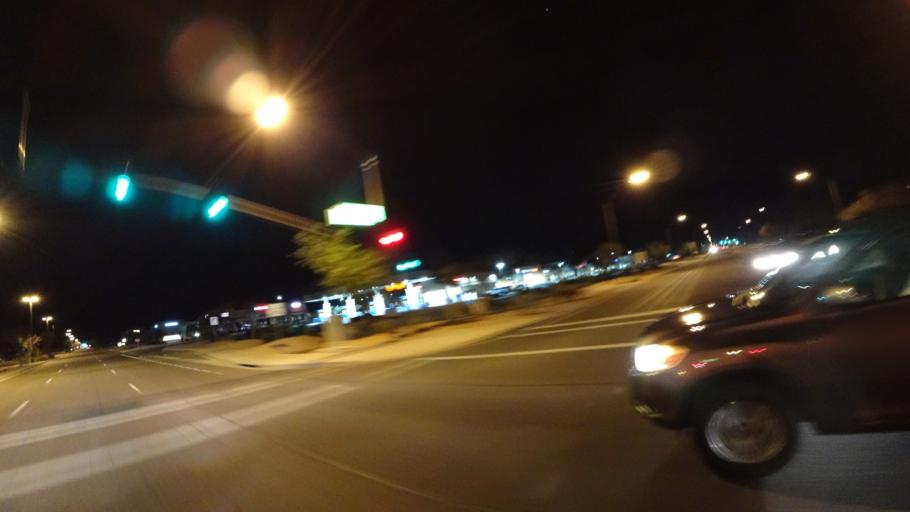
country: US
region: Arizona
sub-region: Maricopa County
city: Gilbert
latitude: 33.3355
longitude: -111.7730
